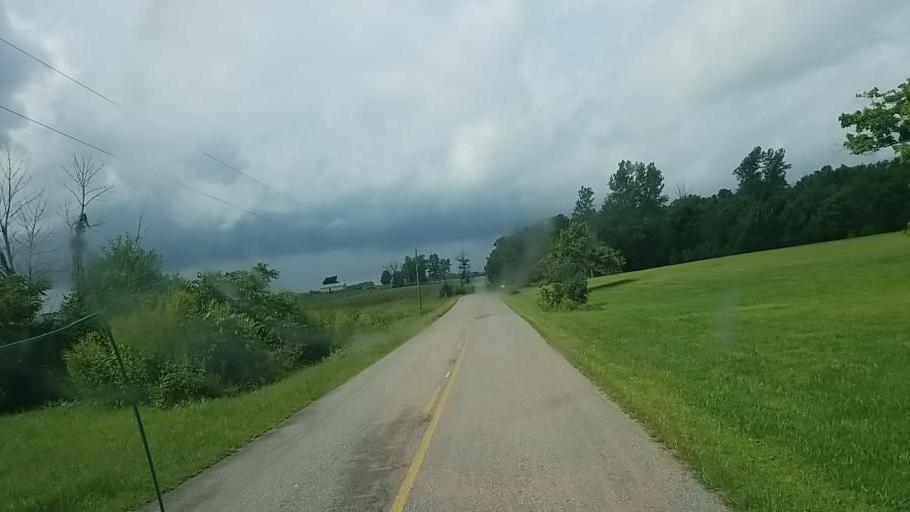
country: US
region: Ohio
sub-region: Champaign County
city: North Lewisburg
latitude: 40.2451
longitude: -83.6486
